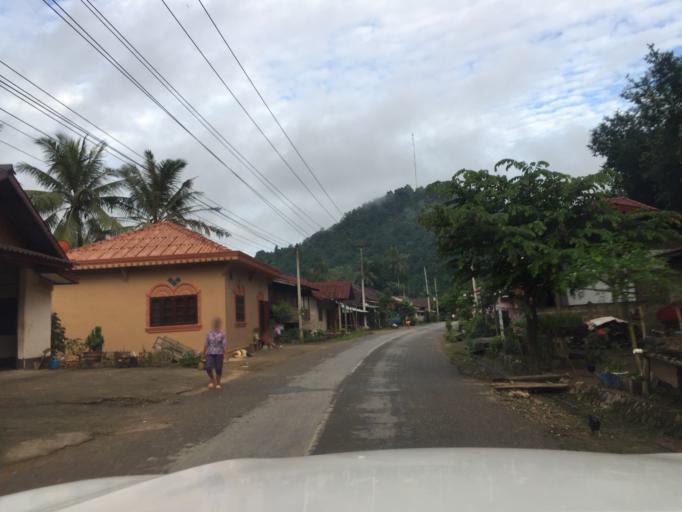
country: LA
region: Phongsali
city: Khoa
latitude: 21.1012
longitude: 102.2608
